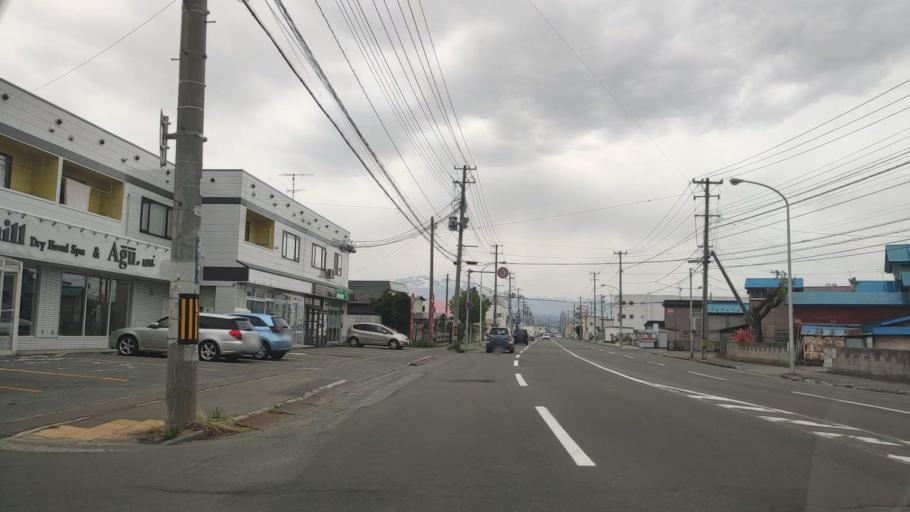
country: JP
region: Aomori
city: Aomori Shi
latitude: 40.8177
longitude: 140.7746
